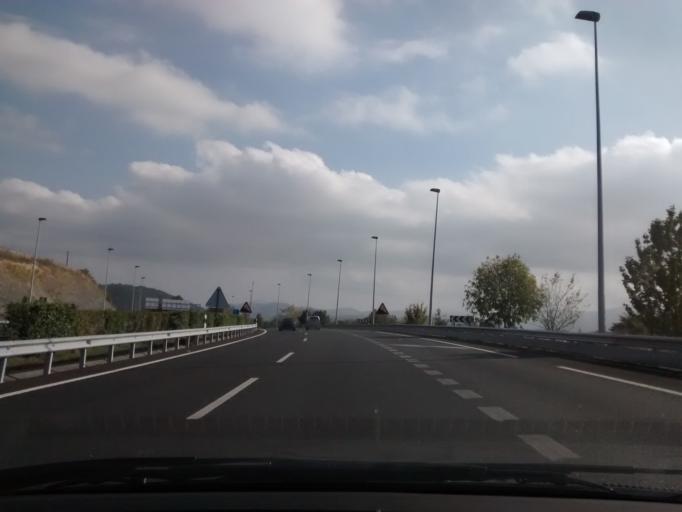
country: ES
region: Cantabria
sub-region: Provincia de Cantabria
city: Lierganes
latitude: 43.3894
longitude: -3.7447
